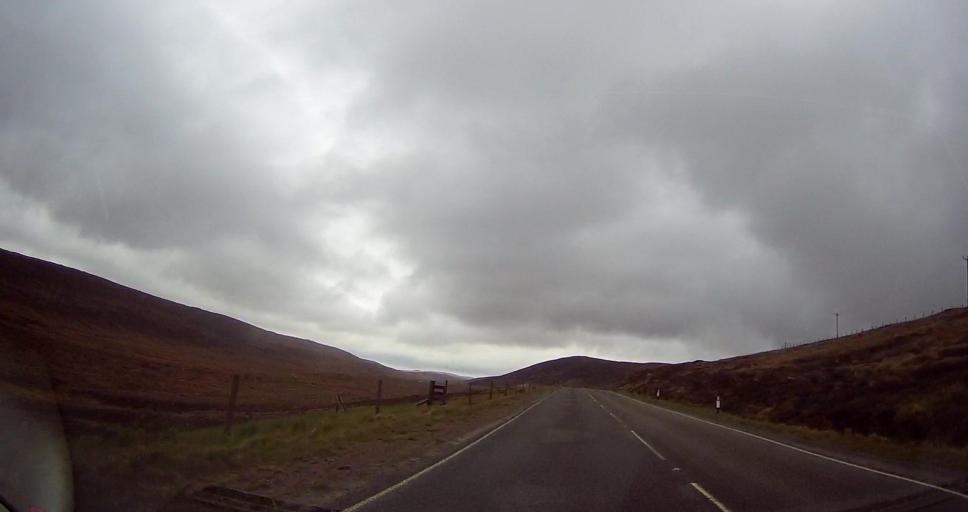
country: GB
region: Scotland
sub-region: Shetland Islands
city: Lerwick
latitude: 60.2947
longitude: -1.2391
